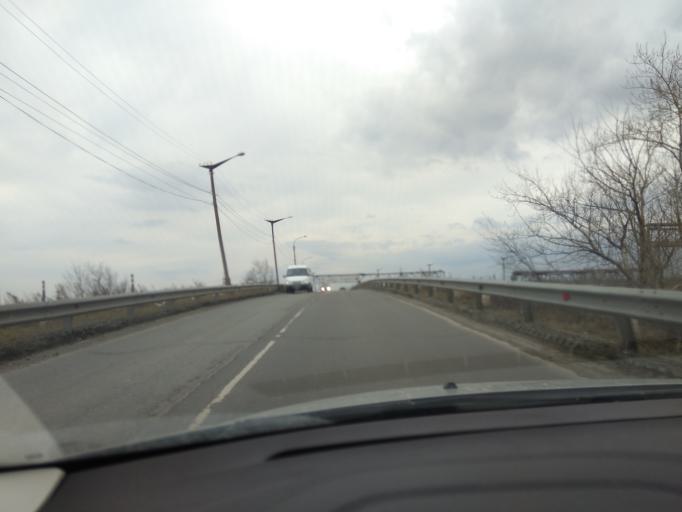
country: RU
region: Chelyabinsk
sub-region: Gorod Chelyabinsk
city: Chelyabinsk
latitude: 55.2489
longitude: 61.4521
